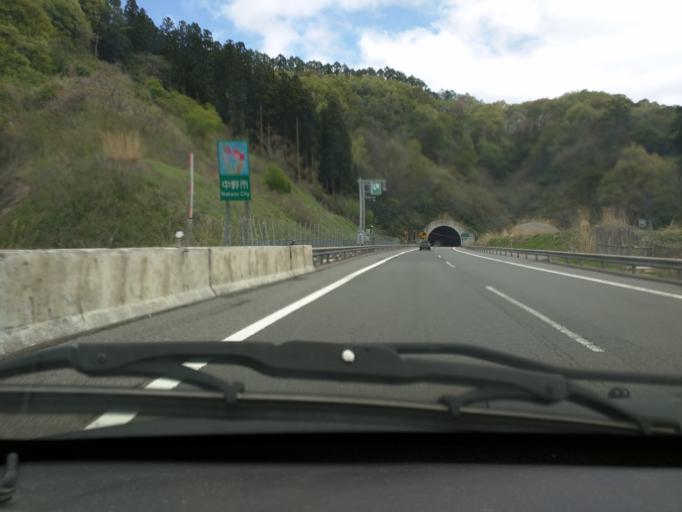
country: JP
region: Nagano
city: Nakano
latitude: 36.7979
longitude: 138.2808
